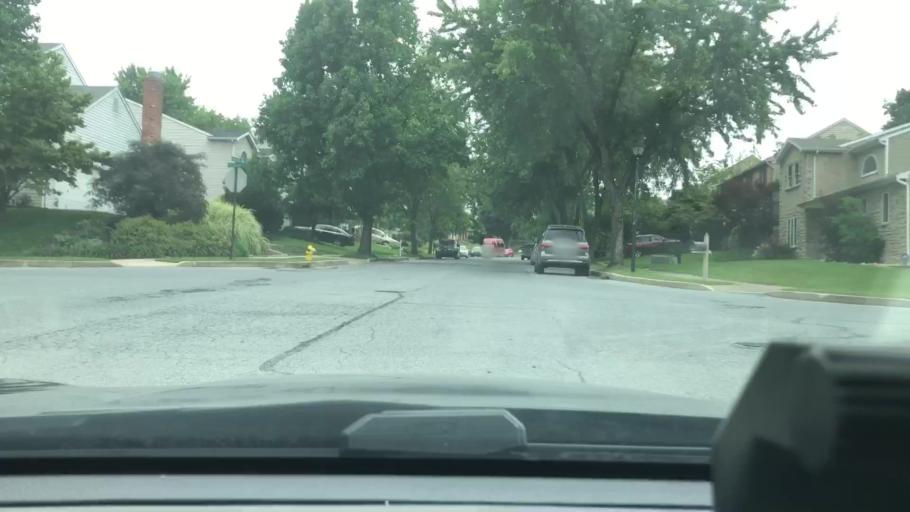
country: US
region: Pennsylvania
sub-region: Lehigh County
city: Allentown
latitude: 40.6186
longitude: -75.4899
